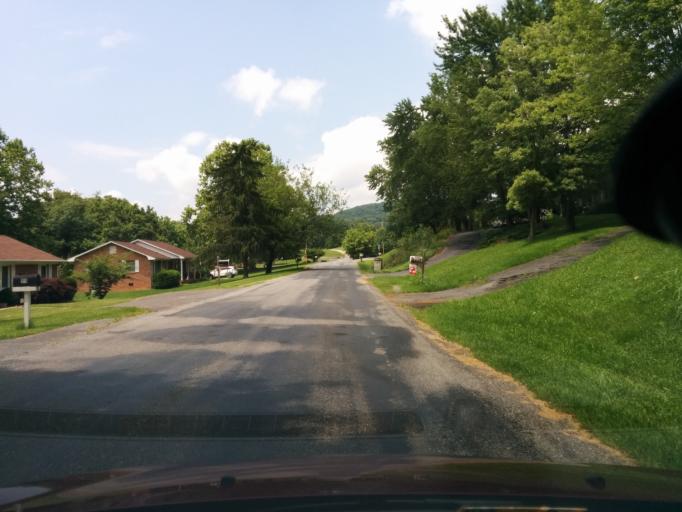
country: US
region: Virginia
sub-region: Rockbridge County
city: East Lexington
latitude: 37.8228
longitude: -79.4002
